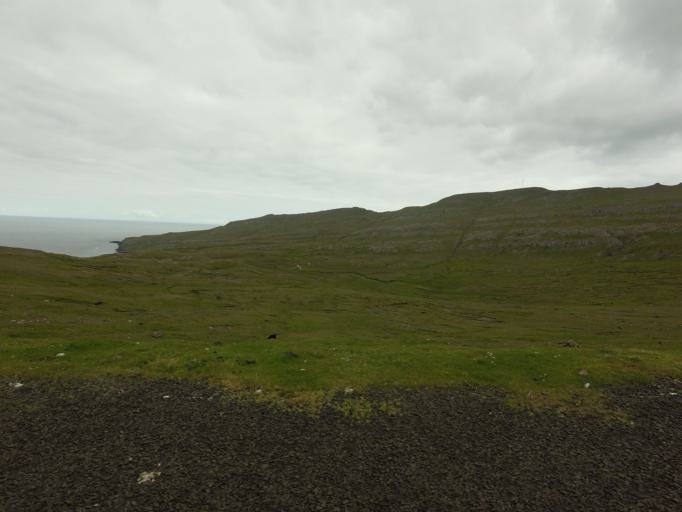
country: FO
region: Suduroy
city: Vagur
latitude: 61.4372
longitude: -6.7548
